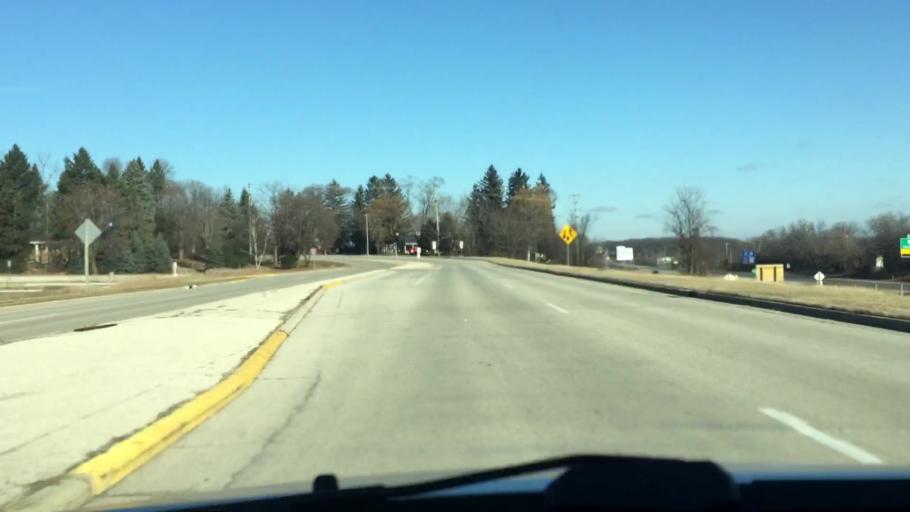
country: US
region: Wisconsin
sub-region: Waukesha County
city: Pewaukee
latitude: 43.0738
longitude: -88.2524
